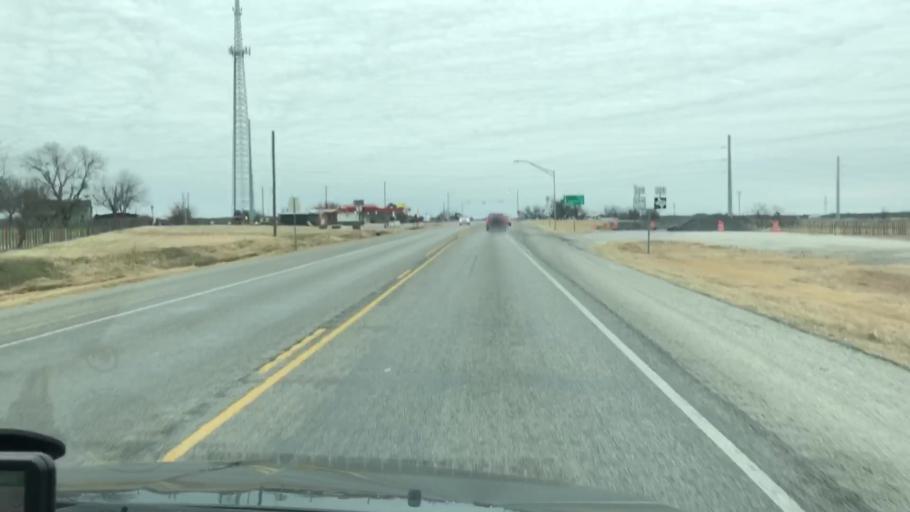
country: US
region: Texas
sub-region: Palo Pinto County
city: Mineral Wells
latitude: 32.9181
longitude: -98.0760
